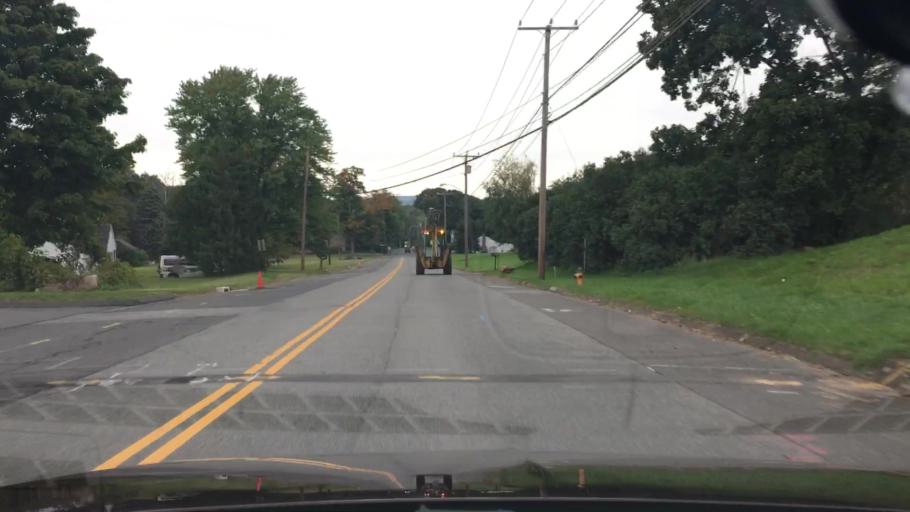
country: US
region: Connecticut
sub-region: Hartford County
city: Kensington
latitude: 41.6015
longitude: -72.7207
